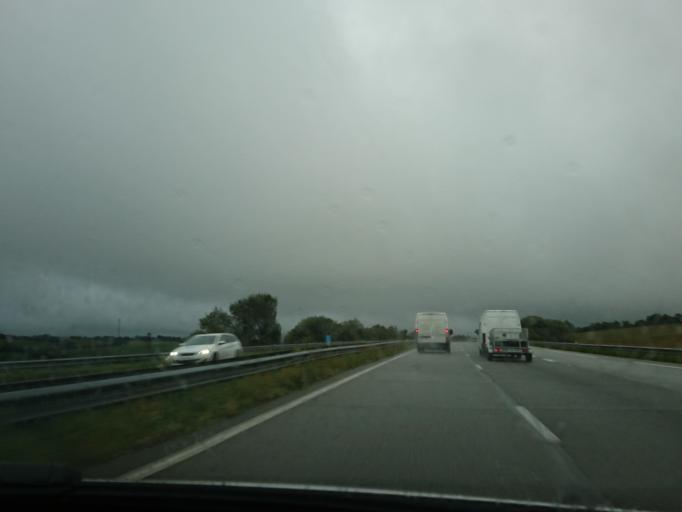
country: FR
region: Brittany
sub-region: Departement du Finistere
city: Chateaulin
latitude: 48.1584
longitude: -4.0404
